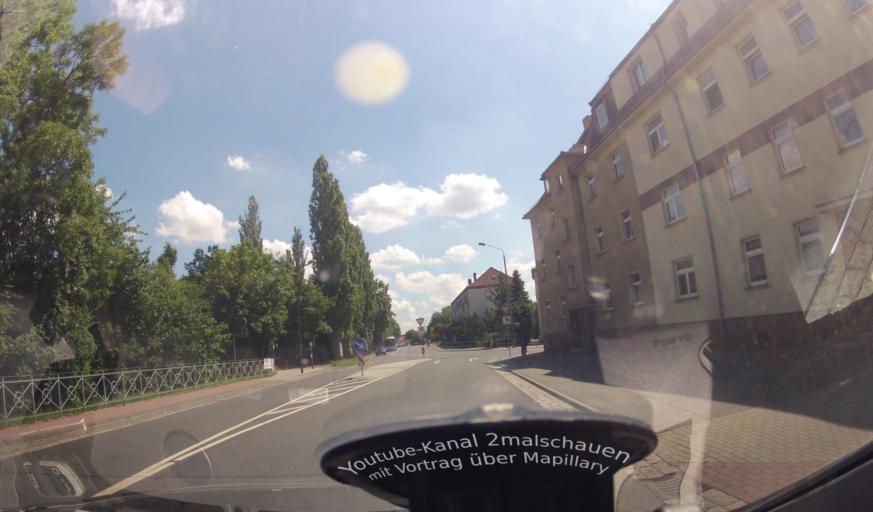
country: DE
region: Saxony
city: Torgau
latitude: 51.5592
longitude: 12.9927
